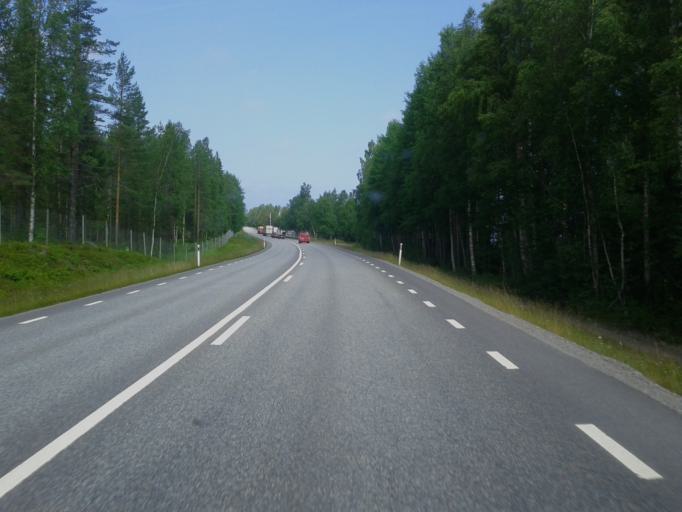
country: SE
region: Vaesterbotten
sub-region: Skelleftea Kommun
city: Burea
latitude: 64.5359
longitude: 21.2586
